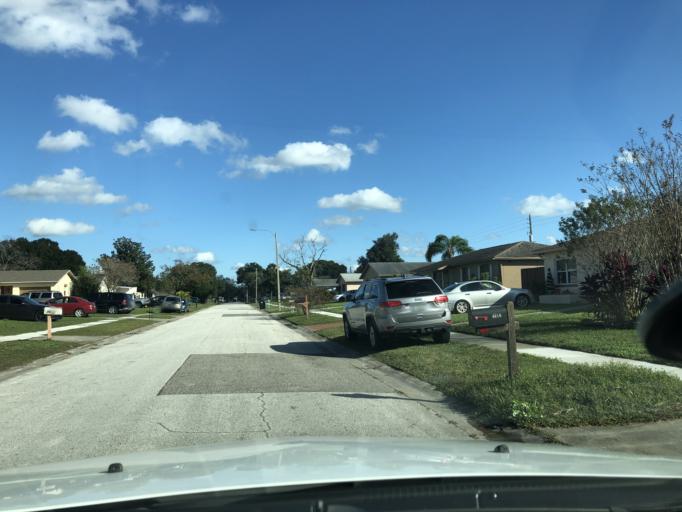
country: US
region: Florida
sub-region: Orange County
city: Oak Ridge
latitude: 28.4765
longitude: -81.4362
